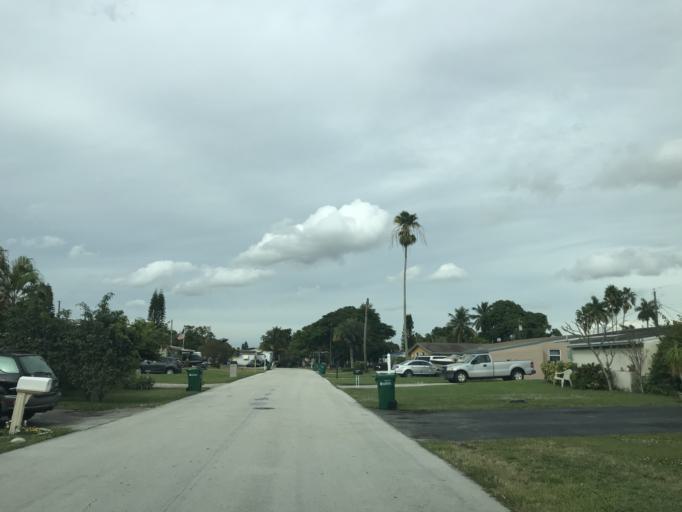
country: US
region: Florida
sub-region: Broward County
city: Margate
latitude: 26.2593
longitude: -80.2078
